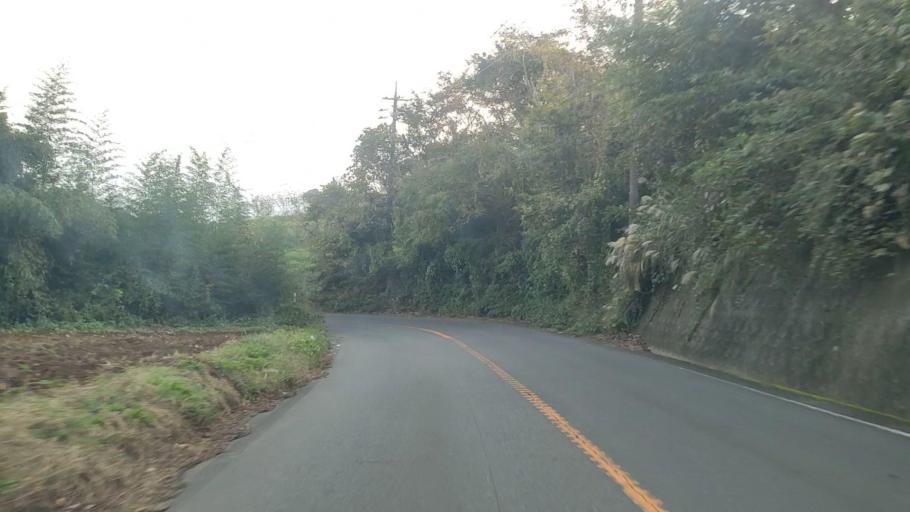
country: JP
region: Shizuoka
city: Mishima
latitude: 35.1542
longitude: 138.9278
